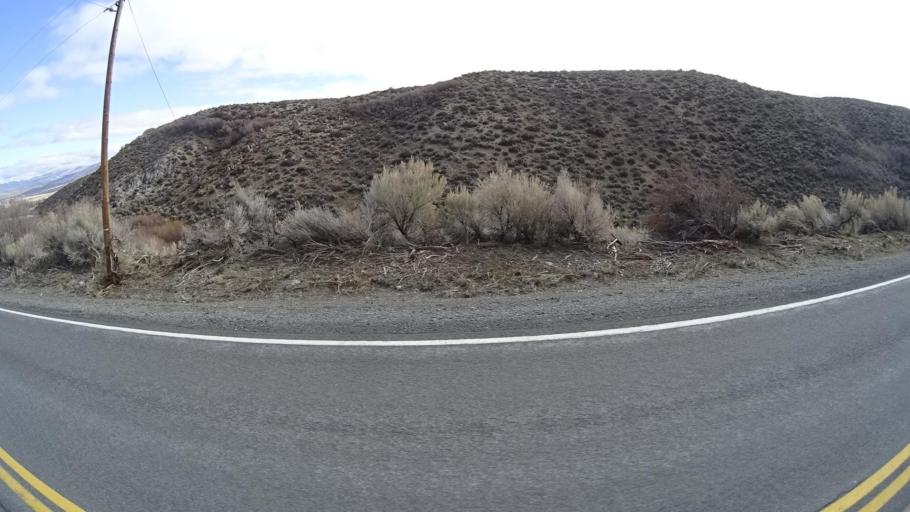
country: US
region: Nevada
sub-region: Washoe County
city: Cold Springs
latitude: 39.8280
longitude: -119.9384
